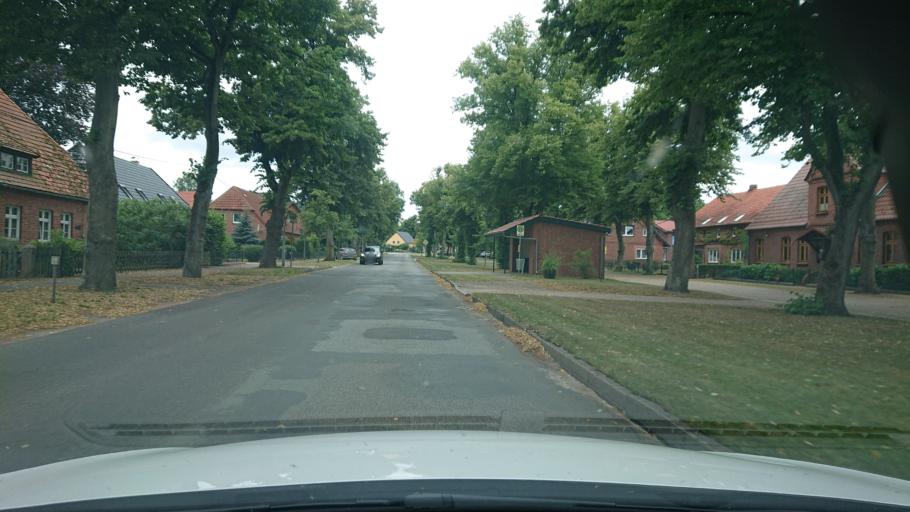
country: DE
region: Mecklenburg-Vorpommern
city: Ludwigslust
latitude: 53.3437
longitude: 11.4107
